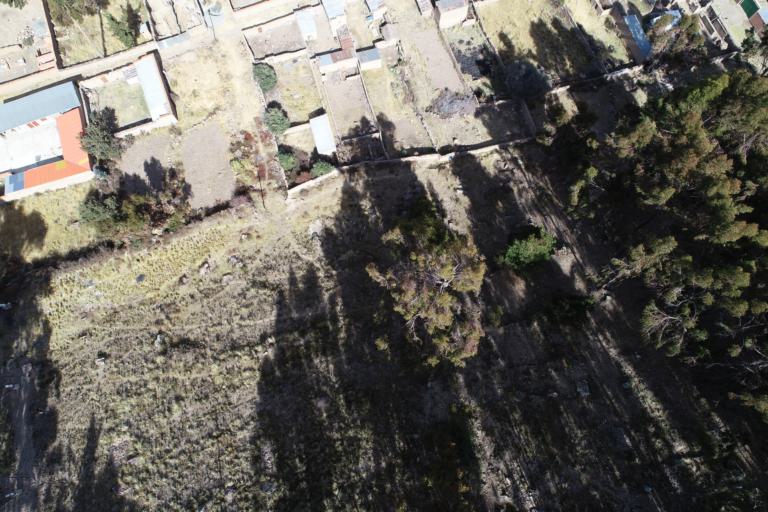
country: BO
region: La Paz
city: Achacachi
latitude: -15.8952
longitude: -68.9054
